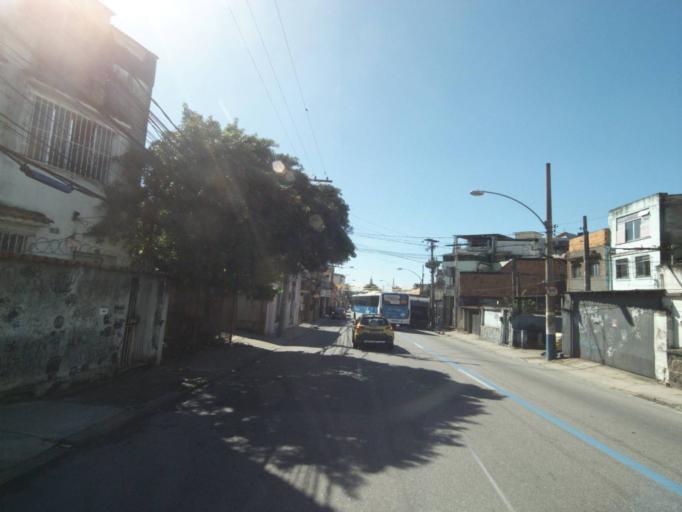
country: BR
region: Rio de Janeiro
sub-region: Rio De Janeiro
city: Rio de Janeiro
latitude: -22.9075
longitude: -43.2719
